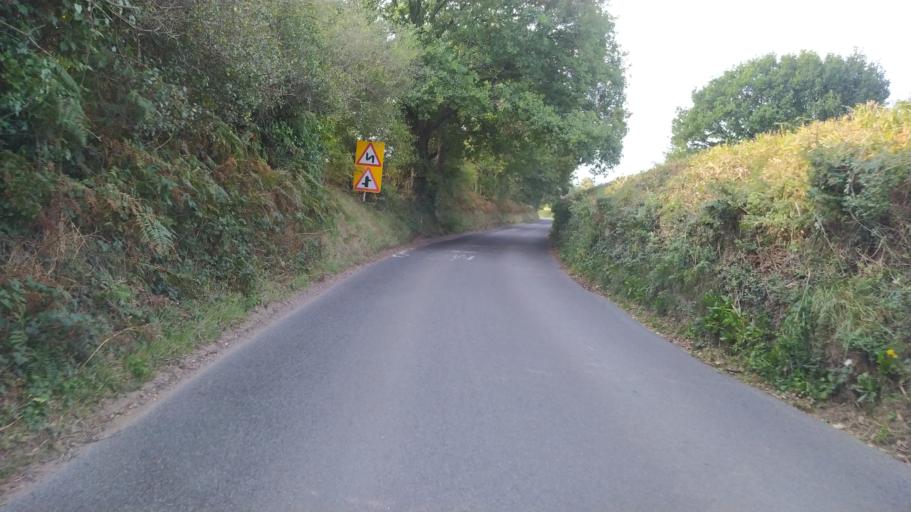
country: GB
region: England
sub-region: Dorset
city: Lytchett Matravers
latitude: 50.7448
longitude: -2.0476
